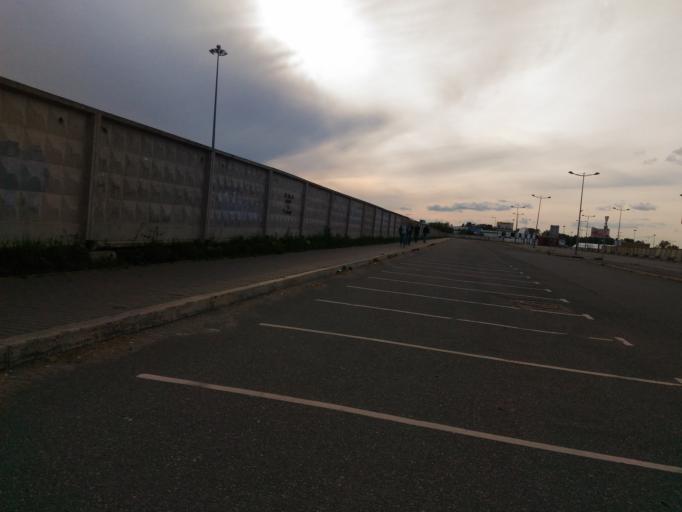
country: RU
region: Ulyanovsk
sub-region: Ulyanovskiy Rayon
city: Ulyanovsk
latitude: 54.2881
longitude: 48.2763
